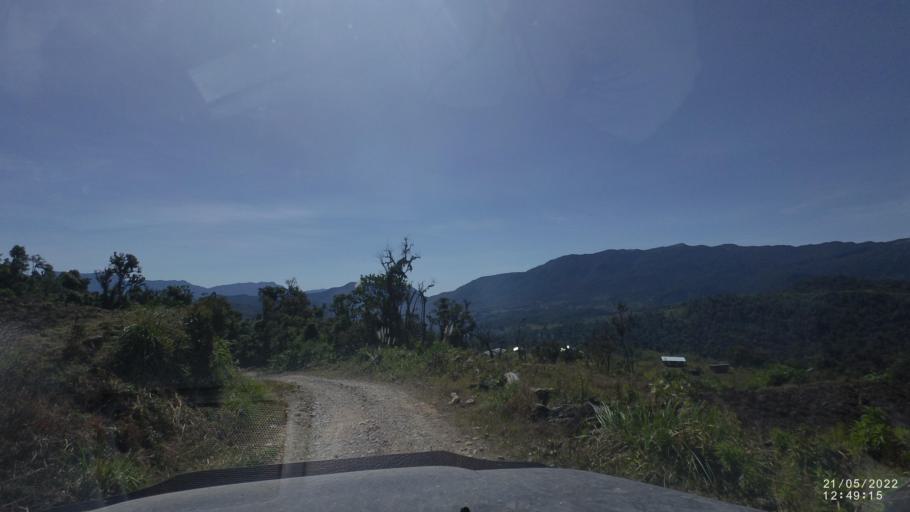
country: BO
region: Cochabamba
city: Colomi
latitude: -17.1790
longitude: -65.9418
